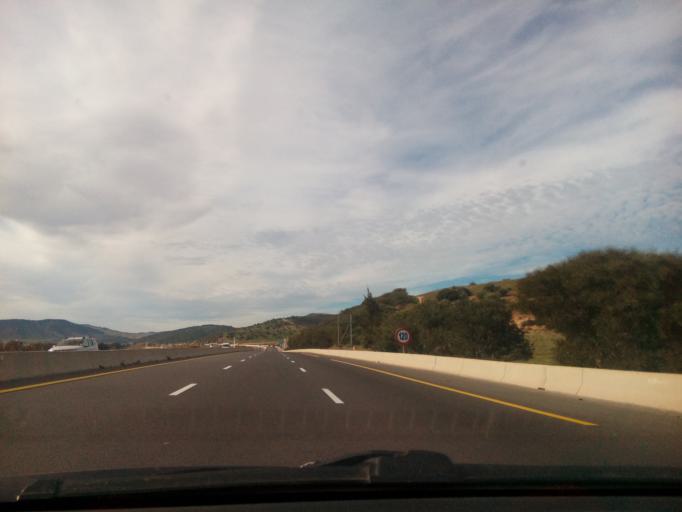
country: DZ
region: Sidi Bel Abbes
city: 'Ain el Berd
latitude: 35.4361
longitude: -0.4479
